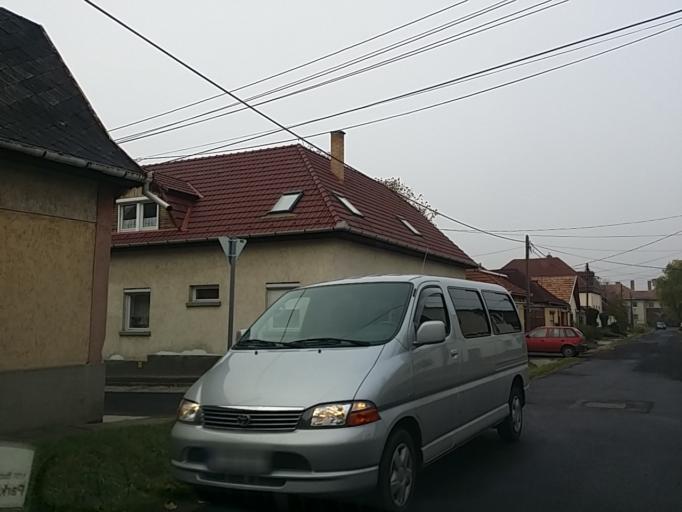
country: HU
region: Heves
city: Gyongyos
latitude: 47.7917
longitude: 19.9323
